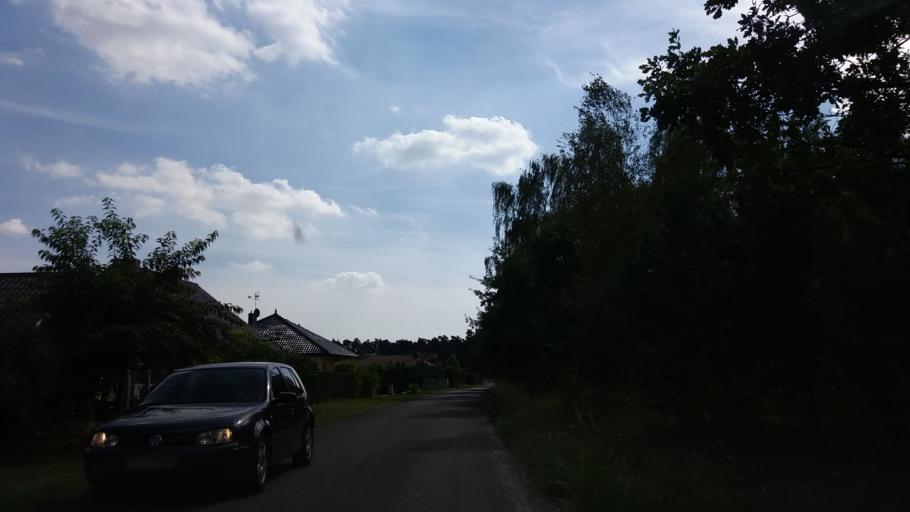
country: PL
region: West Pomeranian Voivodeship
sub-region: Powiat stargardzki
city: Kobylanka
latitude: 53.3547
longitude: 14.9076
